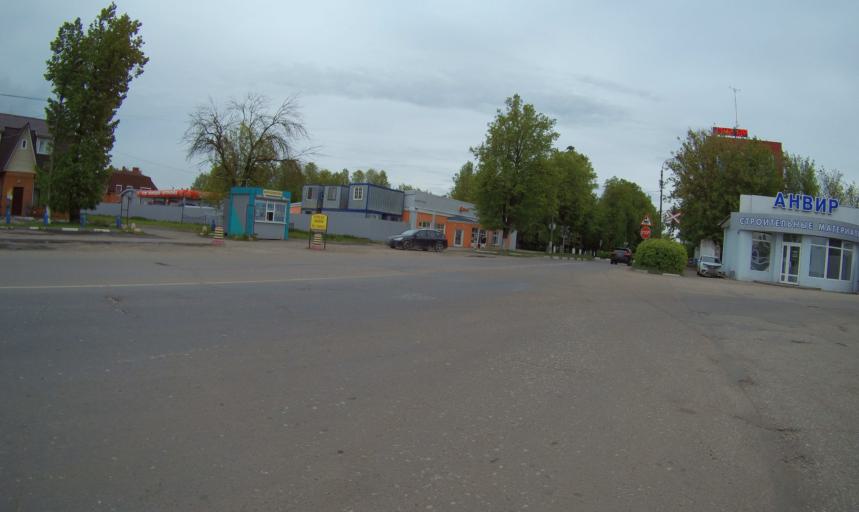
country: RU
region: Moskovskaya
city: Kolomna
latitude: 55.0714
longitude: 38.8032
